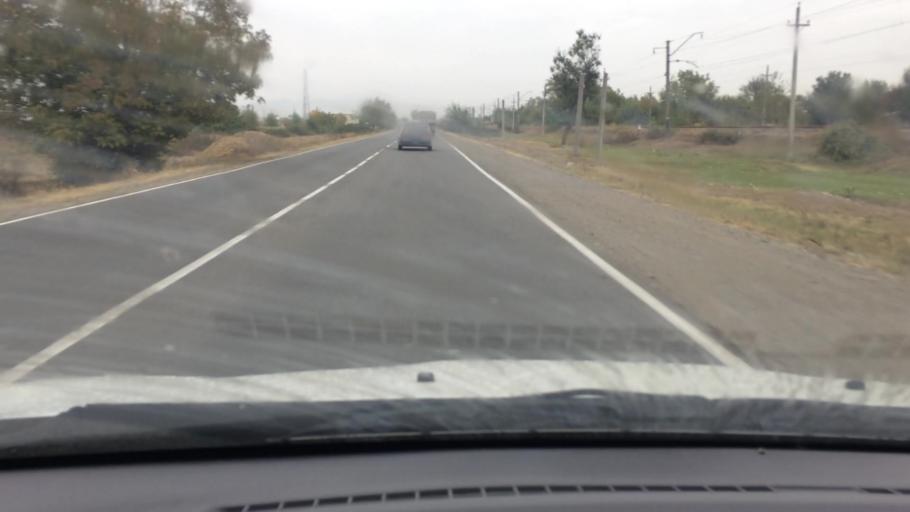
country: GE
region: Kvemo Kartli
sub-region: Marneuli
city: Marneuli
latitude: 41.4308
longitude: 44.8212
